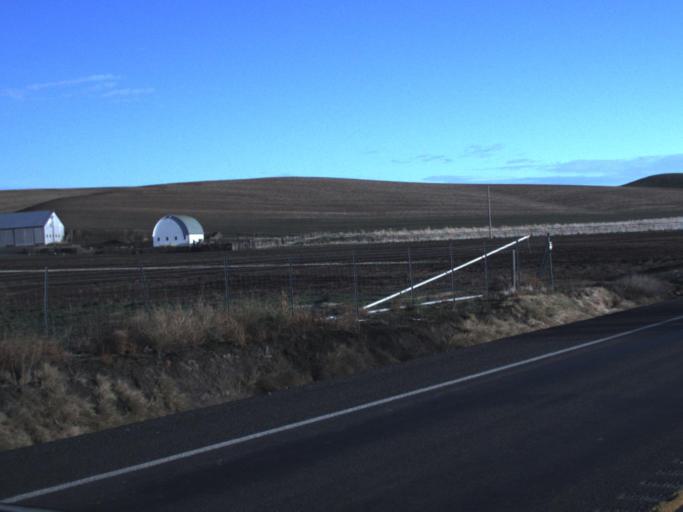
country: US
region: Washington
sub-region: Garfield County
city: Pomeroy
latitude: 46.7914
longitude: -117.6876
